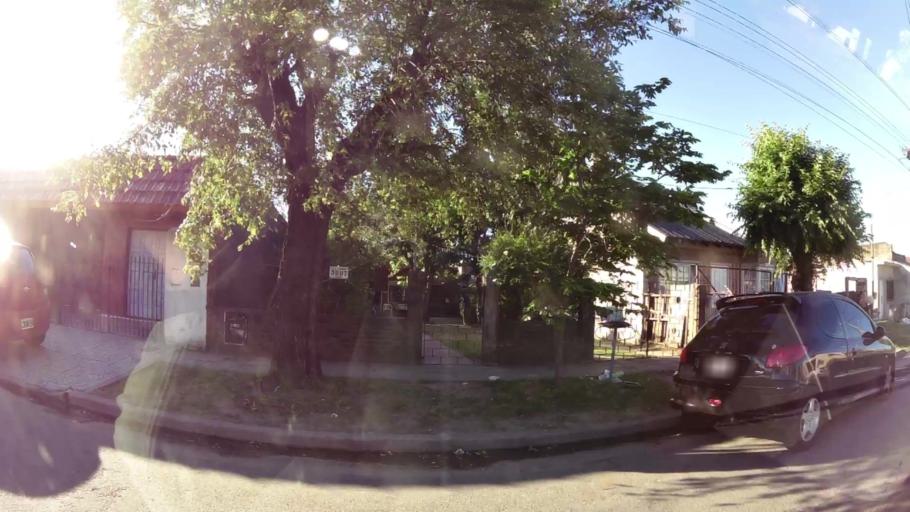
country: AR
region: Buenos Aires
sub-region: Partido de Moron
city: Moron
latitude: -34.6848
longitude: -58.6299
